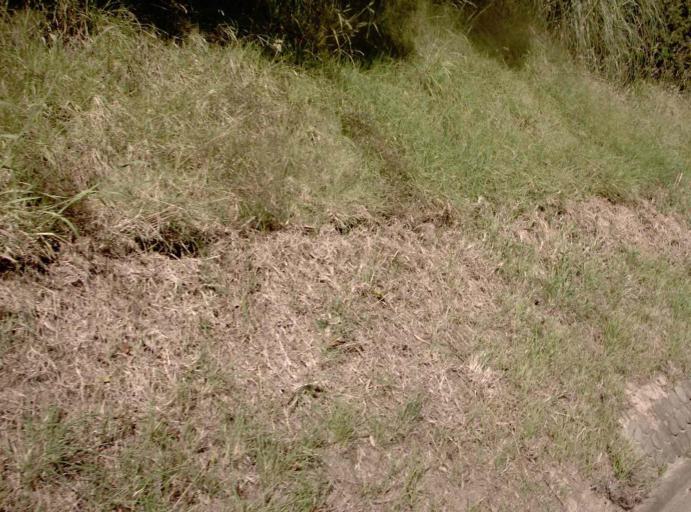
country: AU
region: Victoria
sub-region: East Gippsland
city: Lakes Entrance
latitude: -37.8804
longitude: 147.9631
